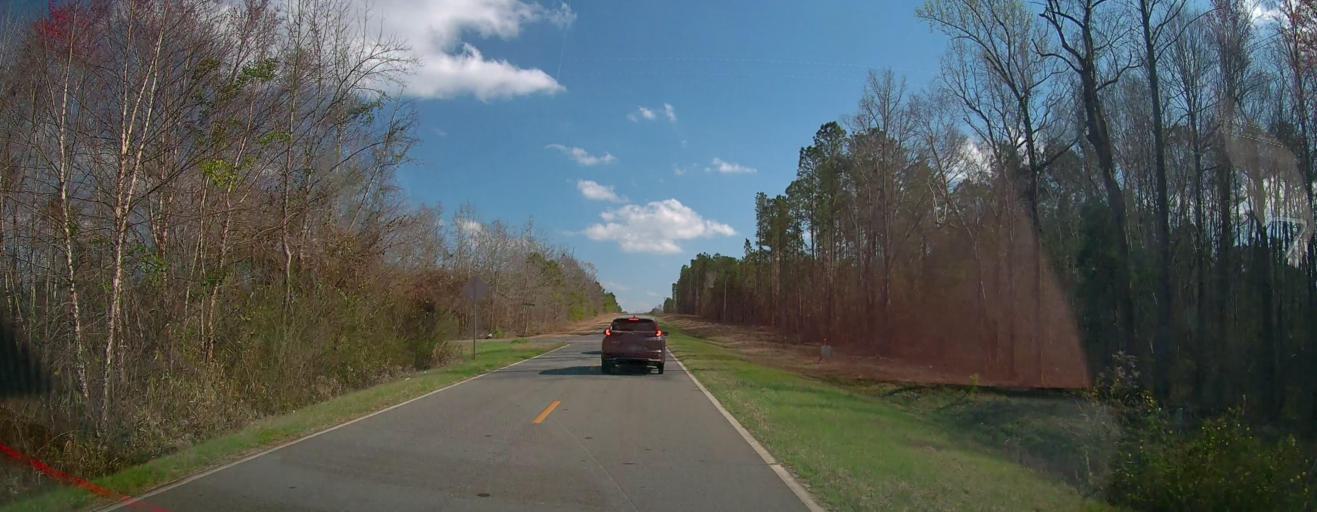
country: US
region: Georgia
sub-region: Laurens County
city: Dublin
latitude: 32.6044
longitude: -83.0758
